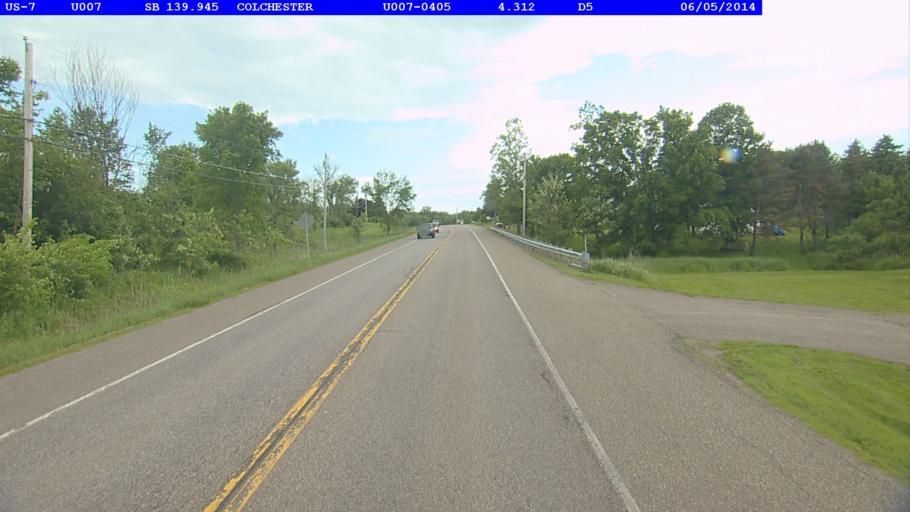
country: US
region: Vermont
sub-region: Chittenden County
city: Colchester
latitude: 44.5607
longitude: -73.1609
